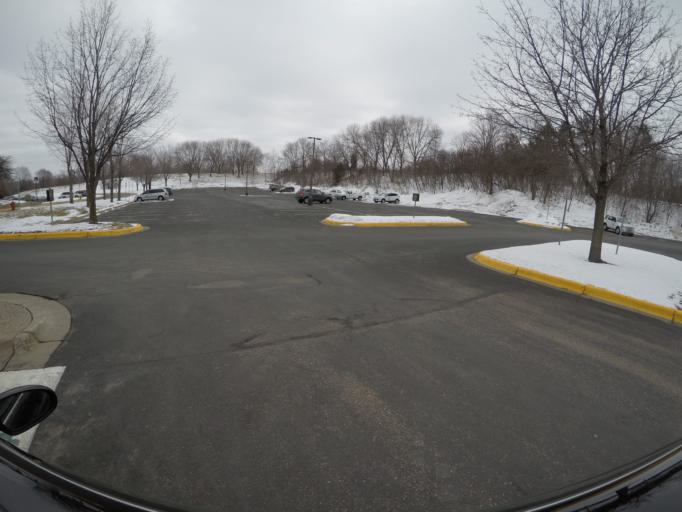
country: US
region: Minnesota
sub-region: Hennepin County
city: Eden Prairie
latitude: 44.8557
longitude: -93.4621
